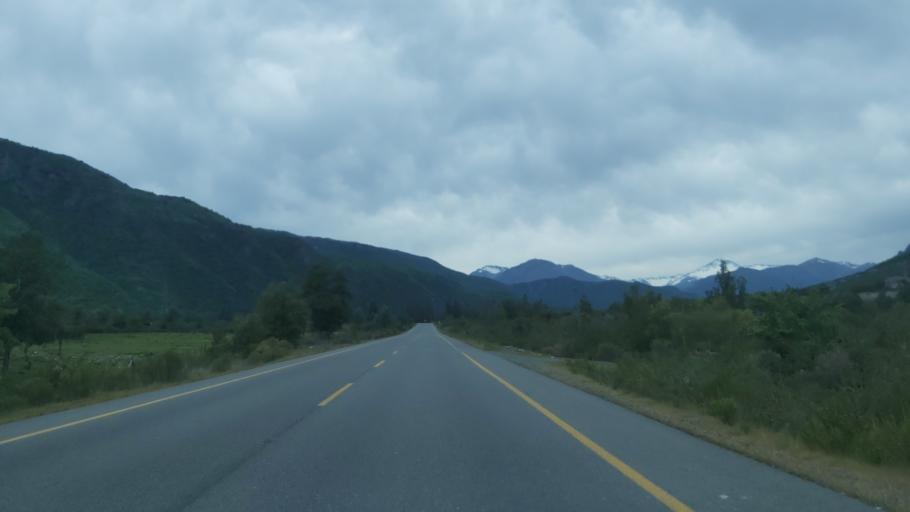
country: CL
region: Maule
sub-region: Provincia de Linares
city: Colbun
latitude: -35.7215
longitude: -71.0296
